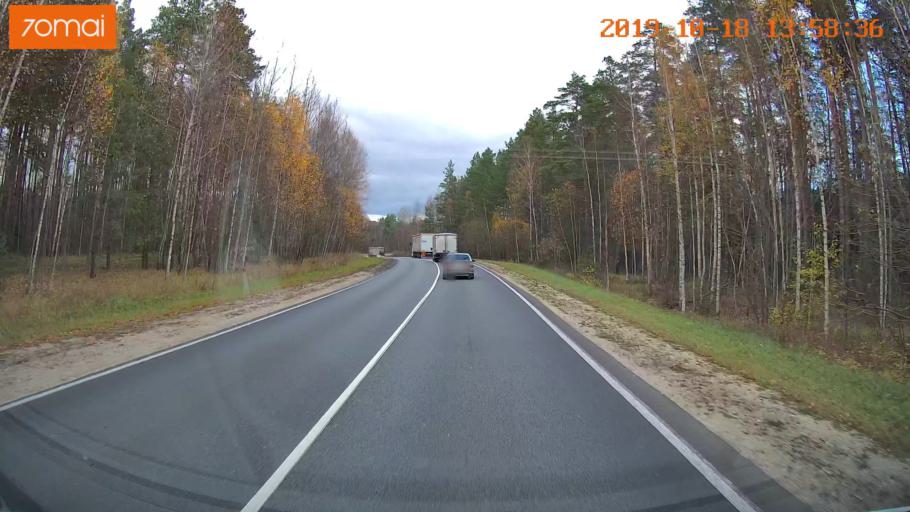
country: RU
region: Rjazan
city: Spas-Klepiki
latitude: 55.0865
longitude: 40.0556
